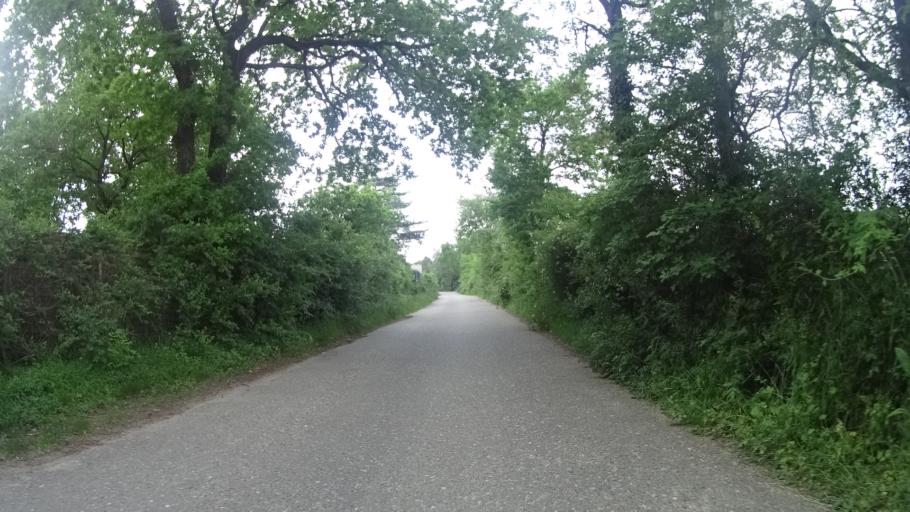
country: DE
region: Baden-Wuerttemberg
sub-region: Freiburg Region
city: Schliengen
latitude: 47.7619
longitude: 7.5479
